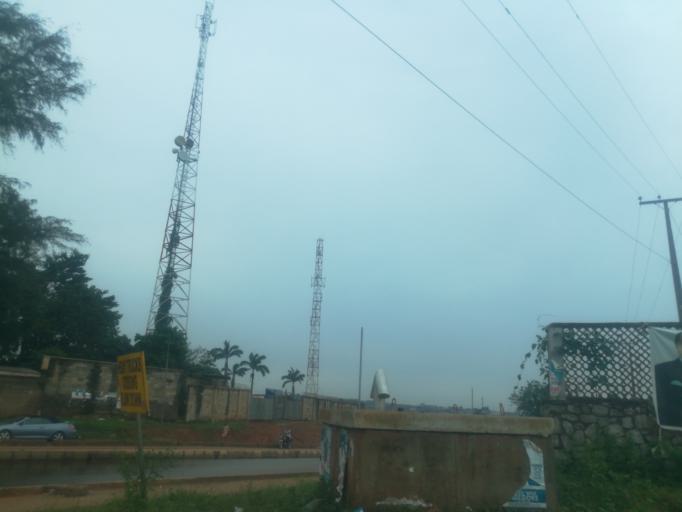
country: NG
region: Oyo
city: Ibadan
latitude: 7.3901
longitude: 3.9323
